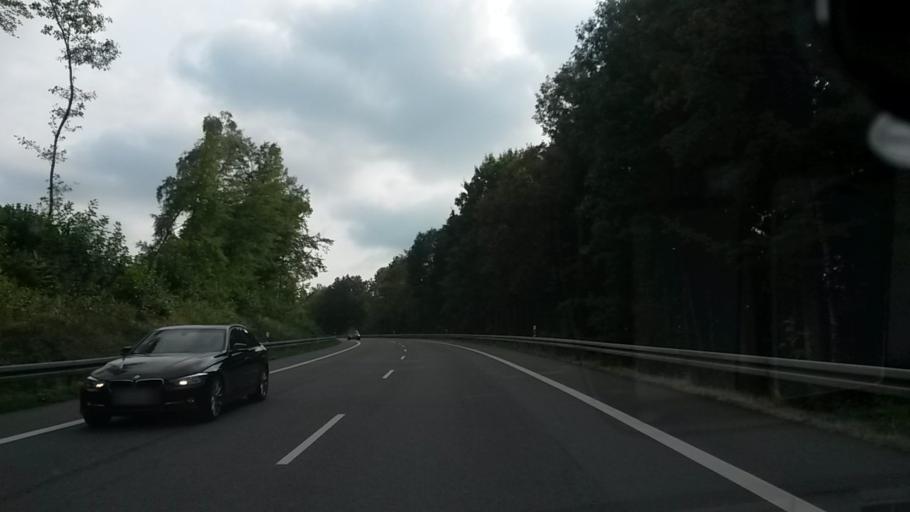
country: DE
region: North Rhine-Westphalia
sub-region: Regierungsbezirk Koln
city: Engelskirchen
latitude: 50.9979
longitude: 7.4278
